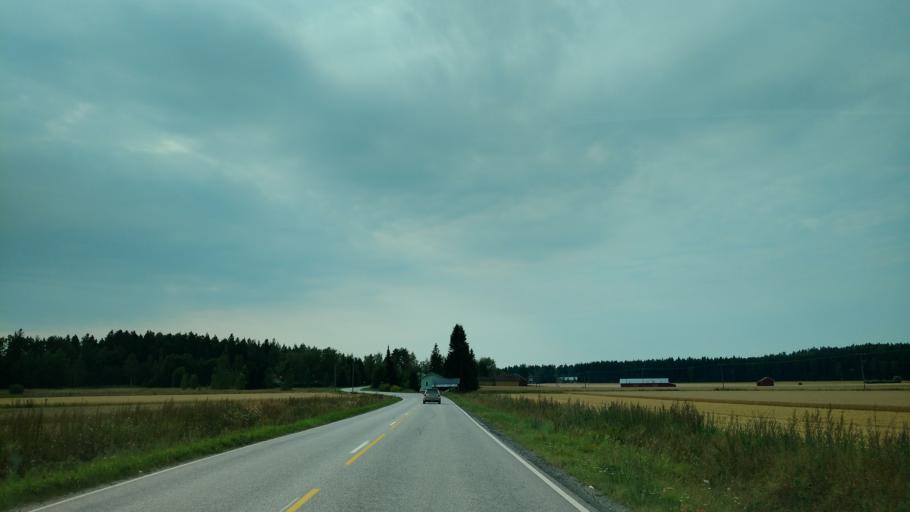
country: FI
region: Varsinais-Suomi
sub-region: Salo
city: Kuusjoki
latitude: 60.4854
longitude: 23.1634
